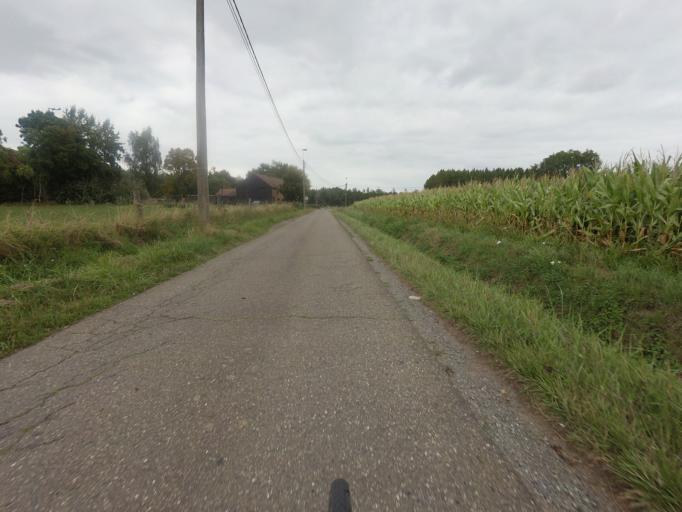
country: BE
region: Flanders
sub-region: Provincie Vlaams-Brabant
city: Bertem
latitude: 50.9031
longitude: 4.5960
